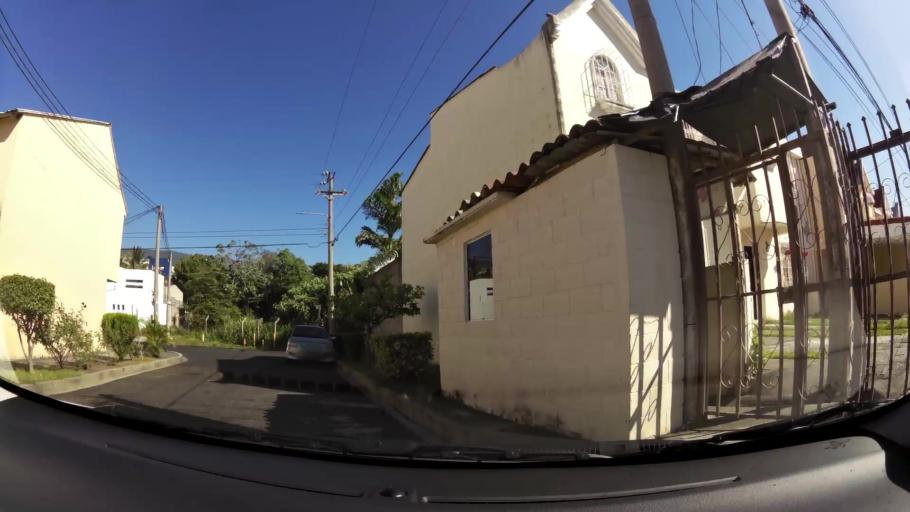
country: SV
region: La Libertad
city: Santa Tecla
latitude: 13.6767
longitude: -89.2743
